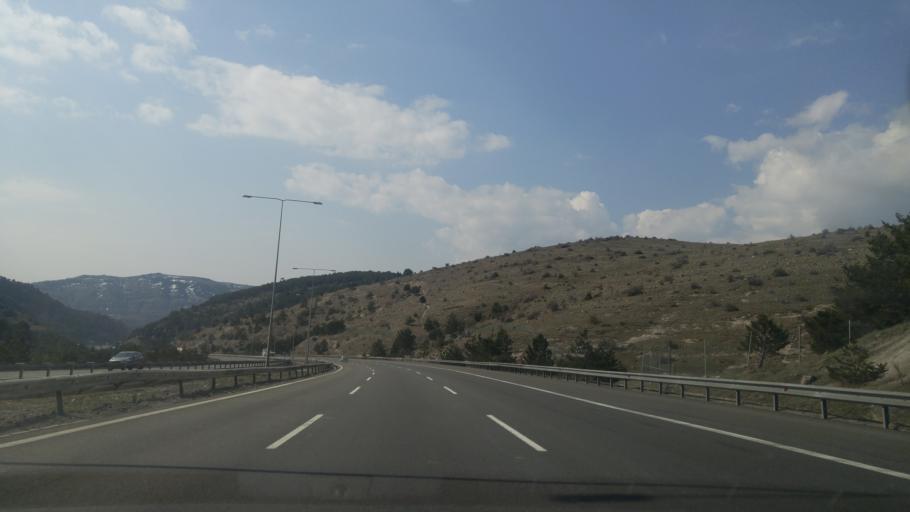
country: TR
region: Ankara
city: Pecenek
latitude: 40.5315
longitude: 32.2878
